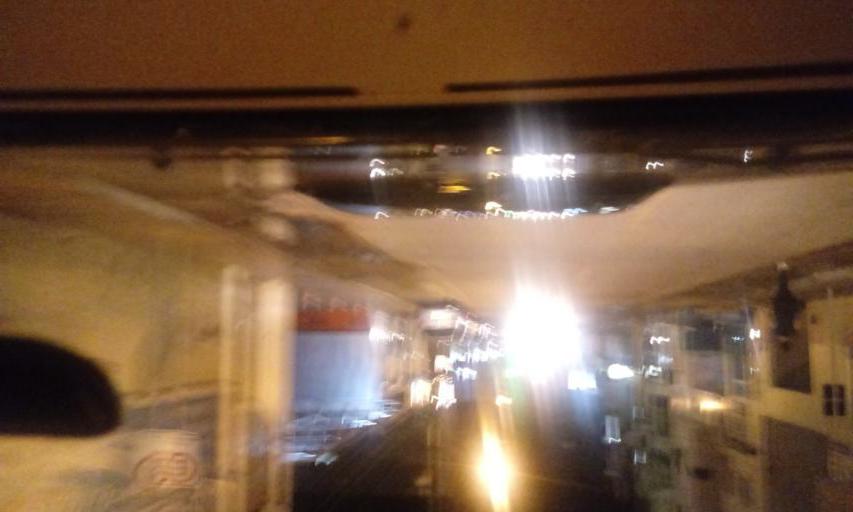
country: BR
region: Bahia
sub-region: Guanambi
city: Guanambi
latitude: -14.2203
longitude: -42.7752
